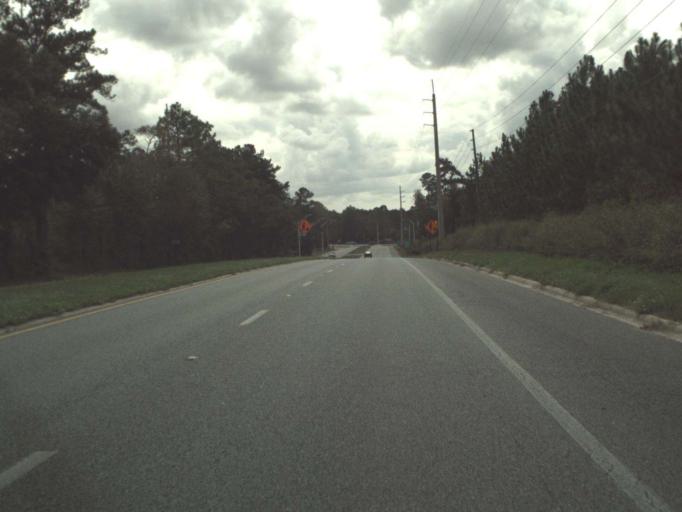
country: US
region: Florida
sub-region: Jefferson County
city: Monticello
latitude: 30.4154
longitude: -83.9112
